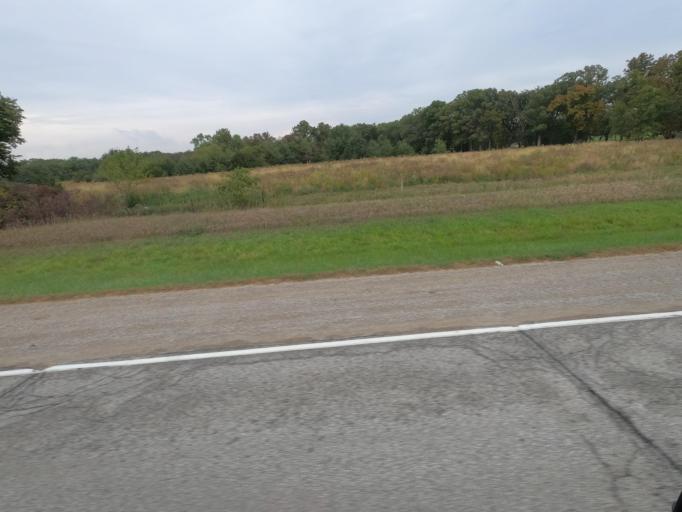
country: US
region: Iowa
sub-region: Van Buren County
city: Keosauqua
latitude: 40.8388
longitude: -92.0073
